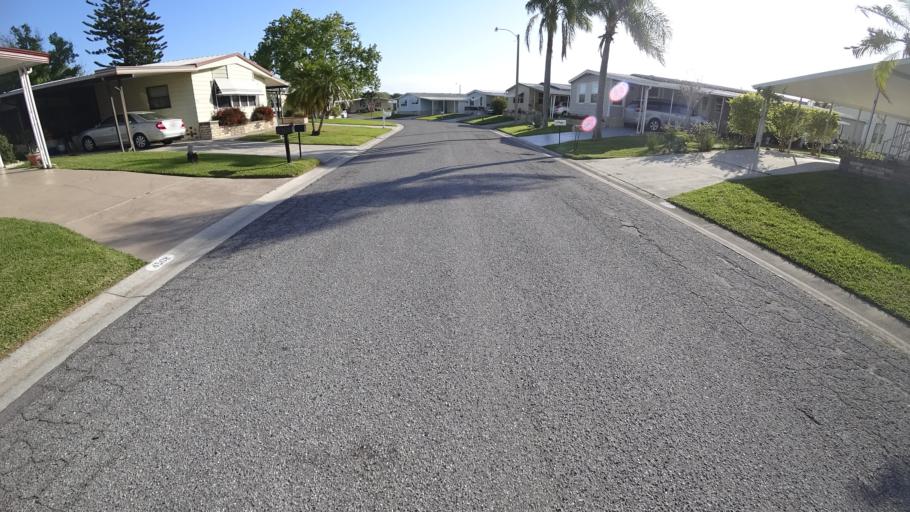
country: US
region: Florida
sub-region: Manatee County
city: Ellenton
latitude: 27.5262
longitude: -82.5185
